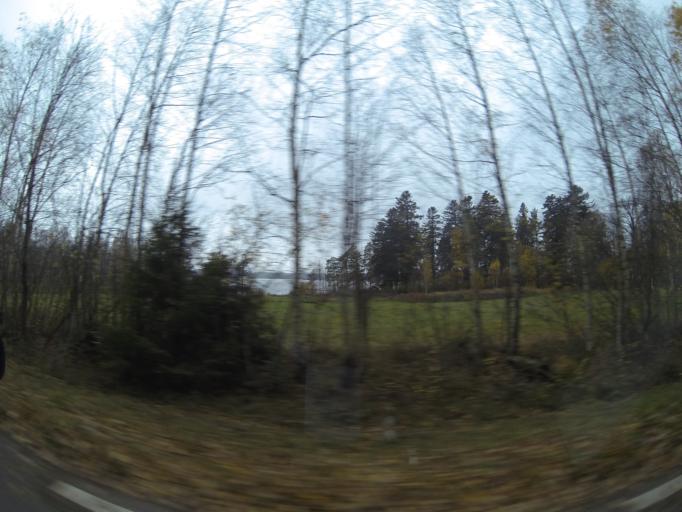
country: SE
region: Vaestmanland
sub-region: Surahammars Kommun
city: Ramnas
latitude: 59.6914
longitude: 16.0828
